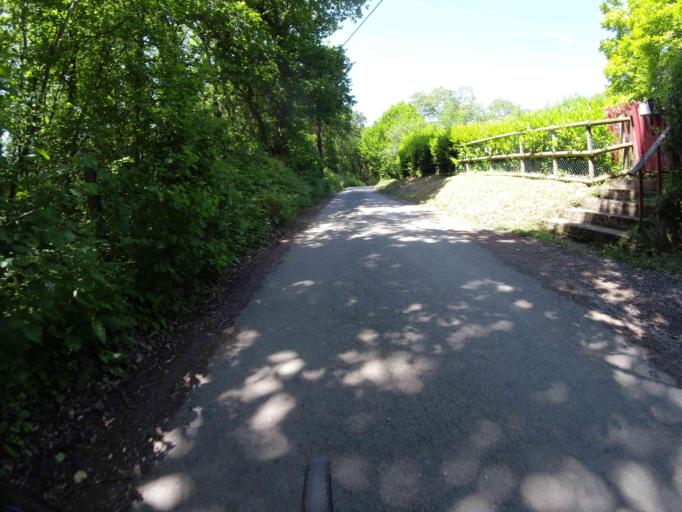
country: GB
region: England
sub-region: Devon
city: Bovey Tracey
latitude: 50.6071
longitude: -3.7067
